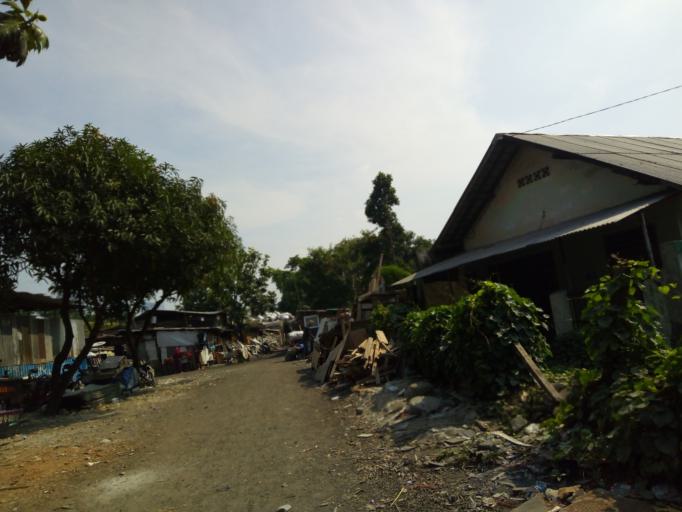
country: ID
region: Jakarta Raya
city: Jakarta
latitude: -6.2074
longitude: 106.8317
